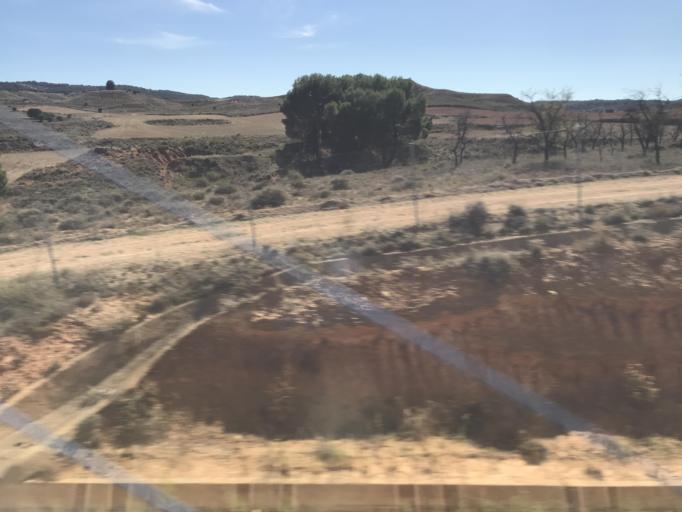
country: ES
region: Aragon
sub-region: Provincia de Zaragoza
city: Contamina
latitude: 41.2781
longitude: -1.9161
